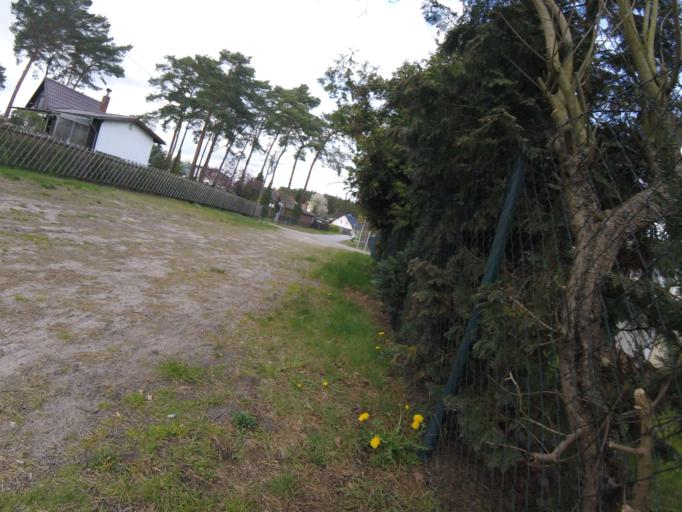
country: DE
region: Brandenburg
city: Bestensee
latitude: 52.2284
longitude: 13.6406
